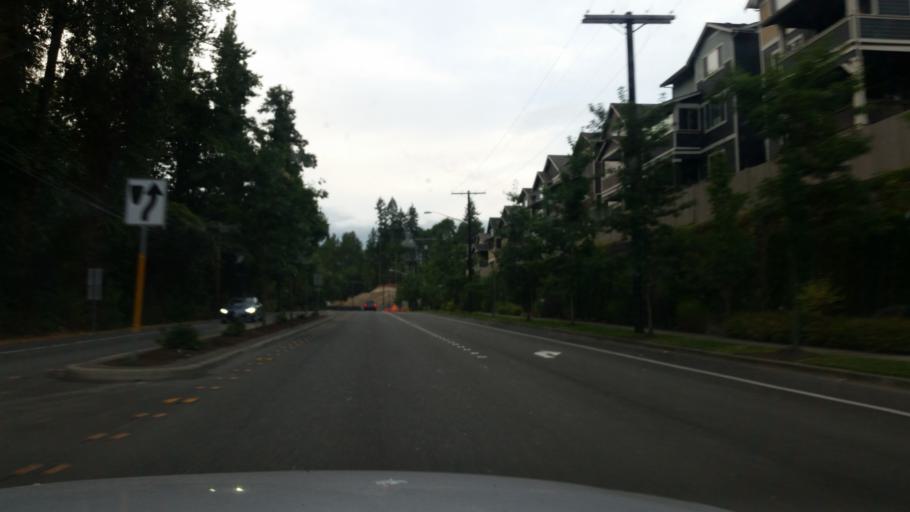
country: US
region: Washington
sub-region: King County
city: Bothell
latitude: 47.7731
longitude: -122.2159
